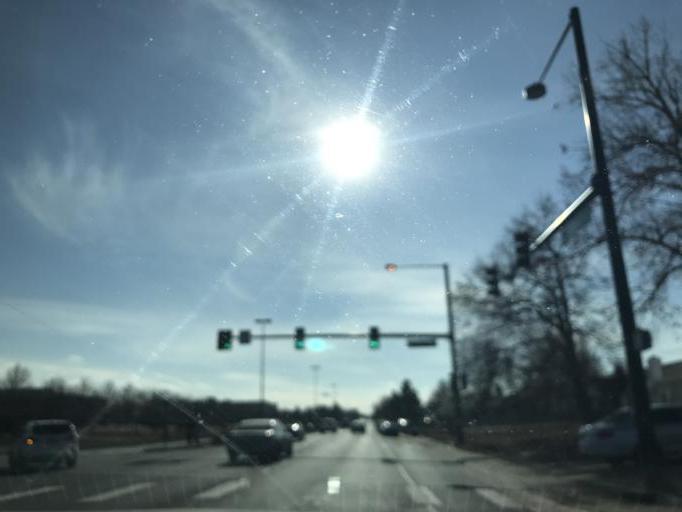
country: US
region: Colorado
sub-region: Adams County
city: Commerce City
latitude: 39.7583
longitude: -104.9036
